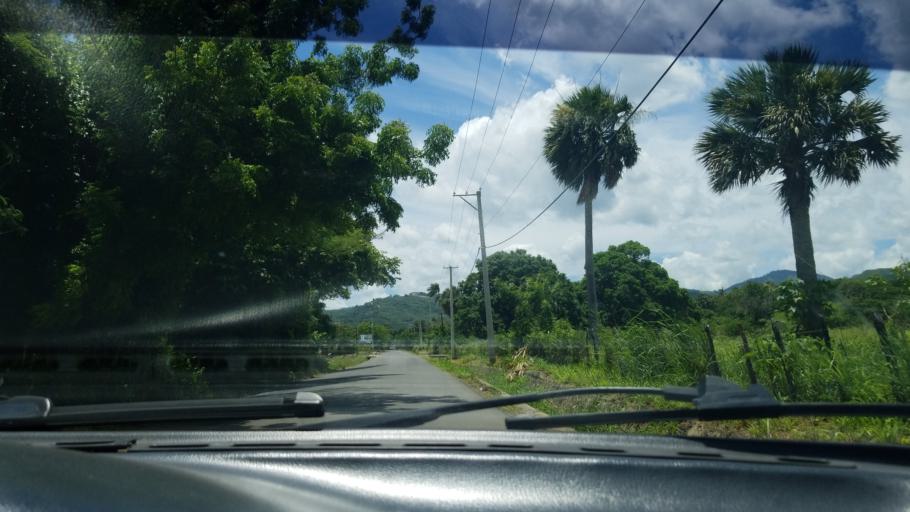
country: DO
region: Santiago
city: Santiago de los Caballeros
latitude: 19.4949
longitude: -70.6767
